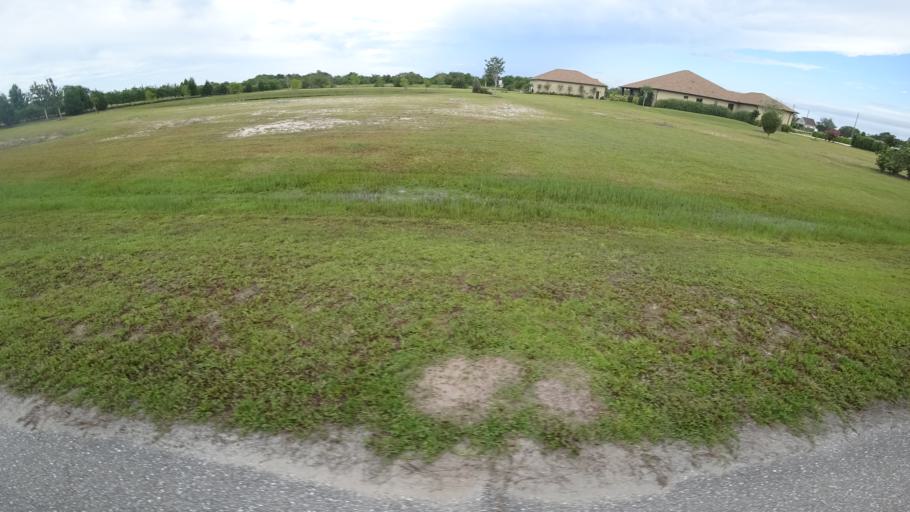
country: US
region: Florida
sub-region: Sarasota County
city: The Meadows
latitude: 27.4221
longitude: -82.2791
